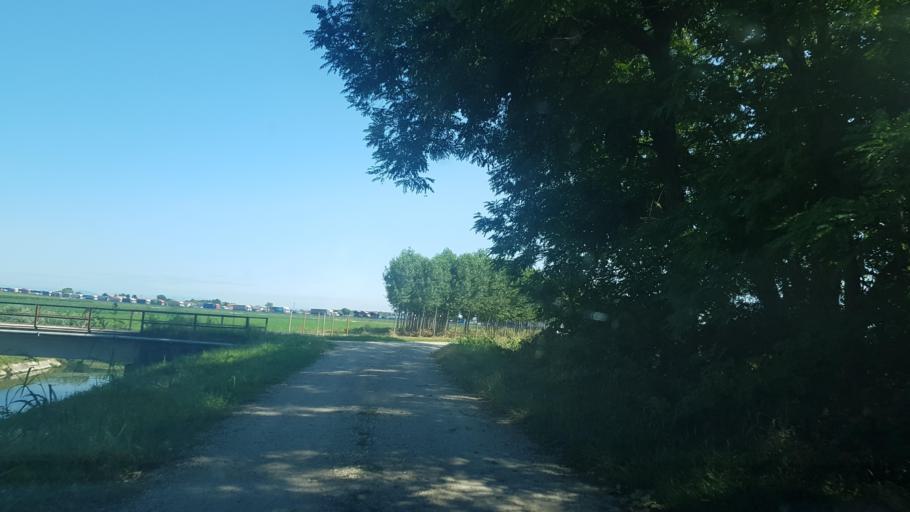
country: IT
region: Friuli Venezia Giulia
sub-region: Provincia di Udine
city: Muzzana del Turgnano
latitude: 45.8442
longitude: 13.1371
